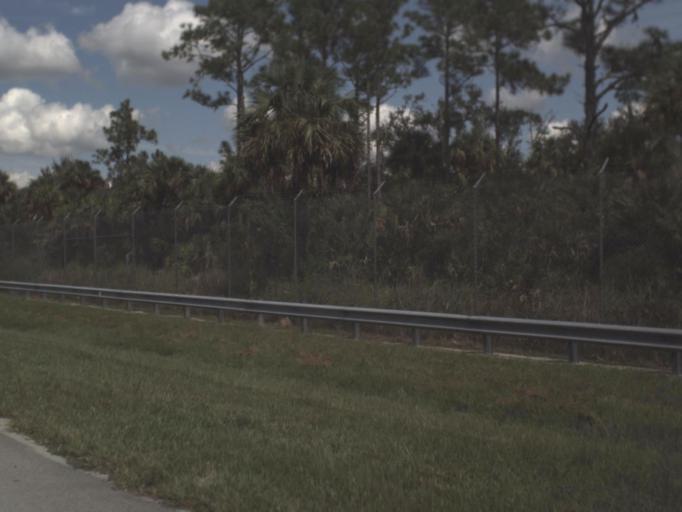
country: US
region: Florida
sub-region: Collier County
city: Immokalee
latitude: 26.1729
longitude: -81.3455
